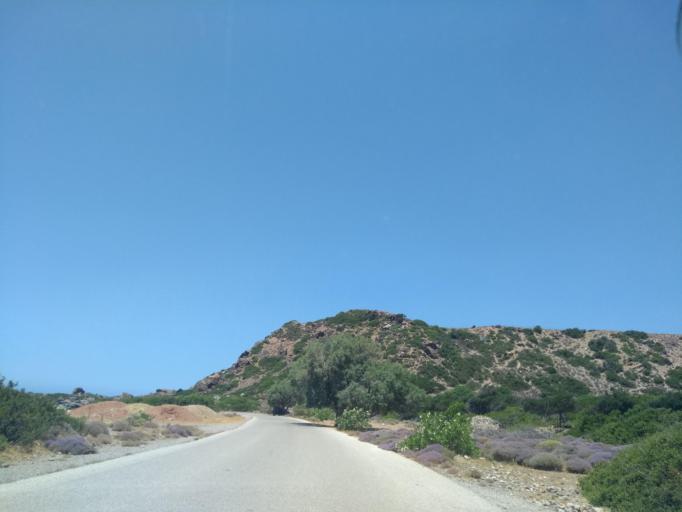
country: GR
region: Crete
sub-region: Nomos Chanias
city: Vryses
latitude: 35.3489
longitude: 23.5388
